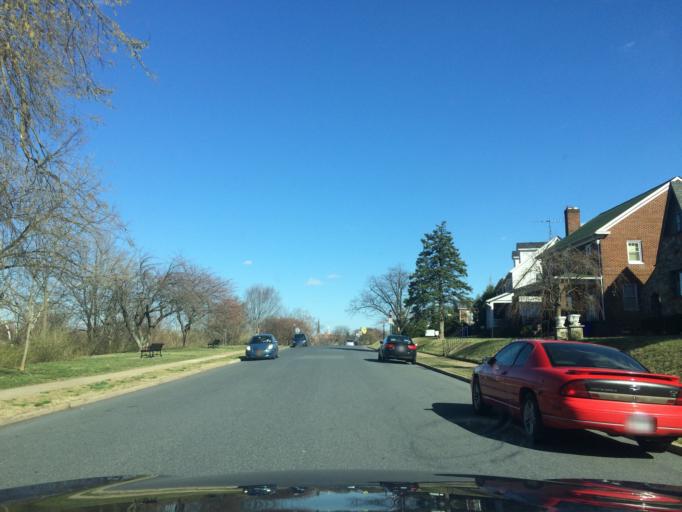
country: US
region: Maryland
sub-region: Frederick County
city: Frederick
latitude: 39.4149
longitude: -77.4220
